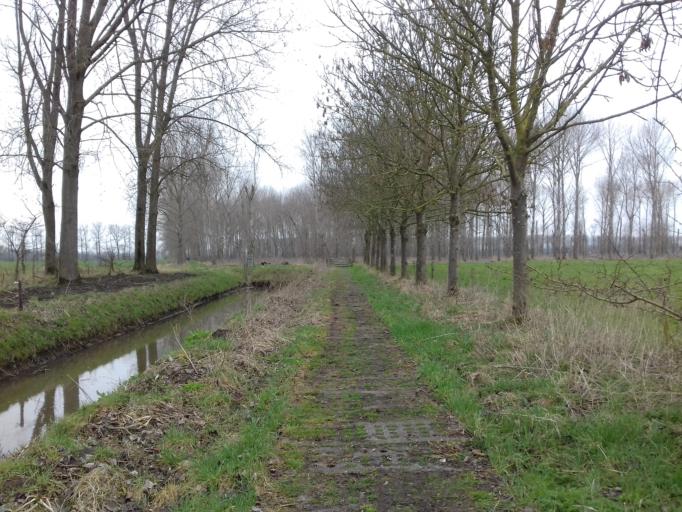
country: NL
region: Gelderland
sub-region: Gemeente Culemborg
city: Culemborg
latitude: 51.9063
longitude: 5.2243
